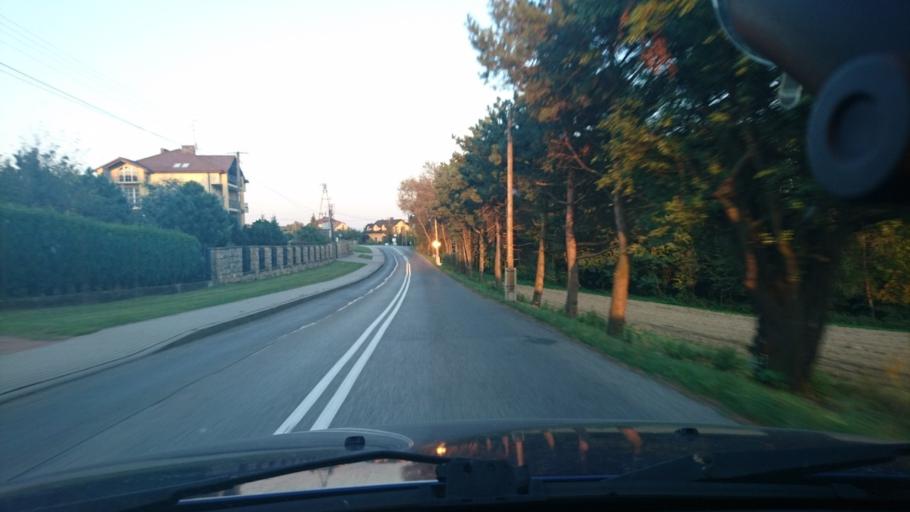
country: PL
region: Silesian Voivodeship
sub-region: Powiat bielski
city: Bestwina
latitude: 49.9011
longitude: 19.0779
